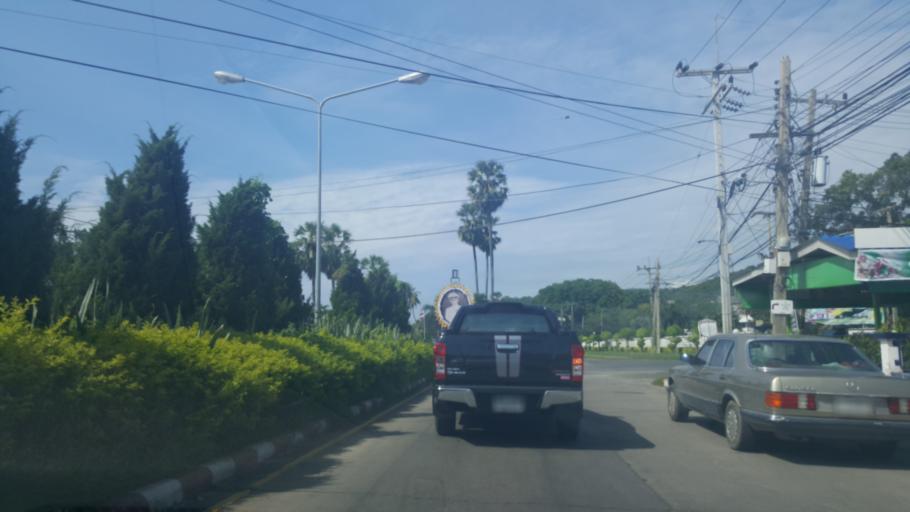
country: TH
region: Chon Buri
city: Sattahip
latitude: 12.6621
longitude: 100.8975
